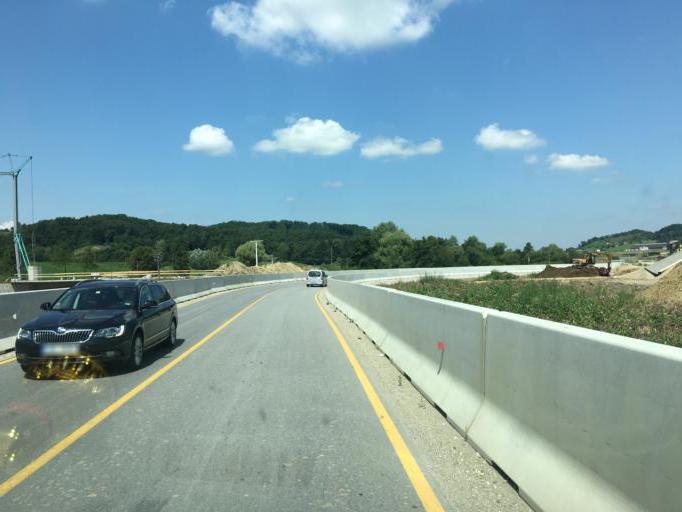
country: SI
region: Podlehnik
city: Podlehnik
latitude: 46.3335
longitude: 15.8767
